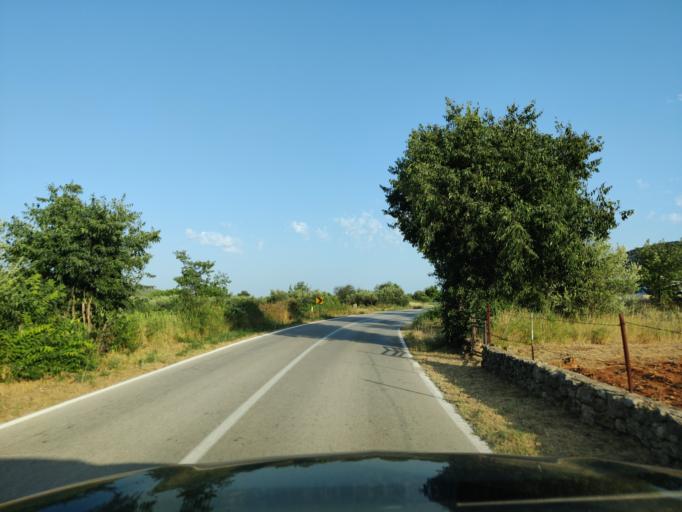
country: HR
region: Sibensko-Kniniska
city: Tribunj
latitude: 43.7797
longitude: 15.7161
